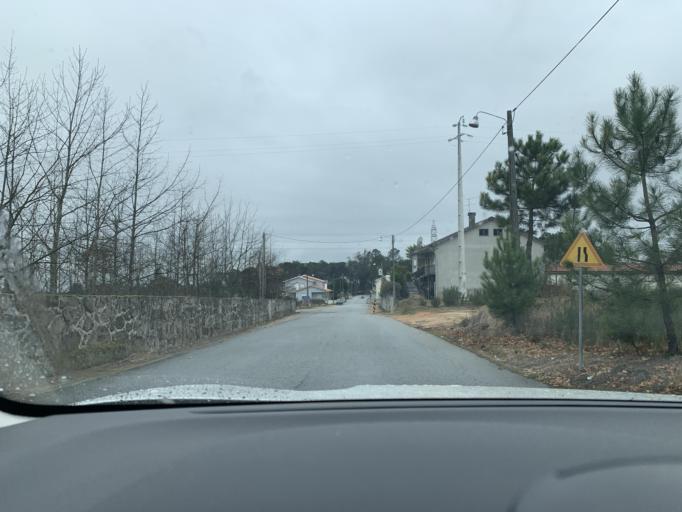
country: PT
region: Viseu
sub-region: Nelas
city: Nelas
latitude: 40.5919
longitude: -7.8403
